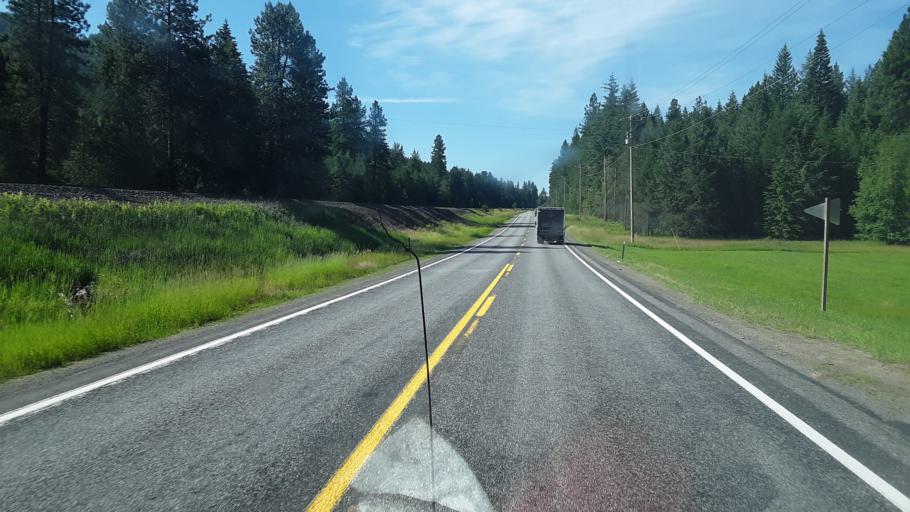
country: US
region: Idaho
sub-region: Boundary County
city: Bonners Ferry
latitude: 48.5123
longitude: -116.4440
